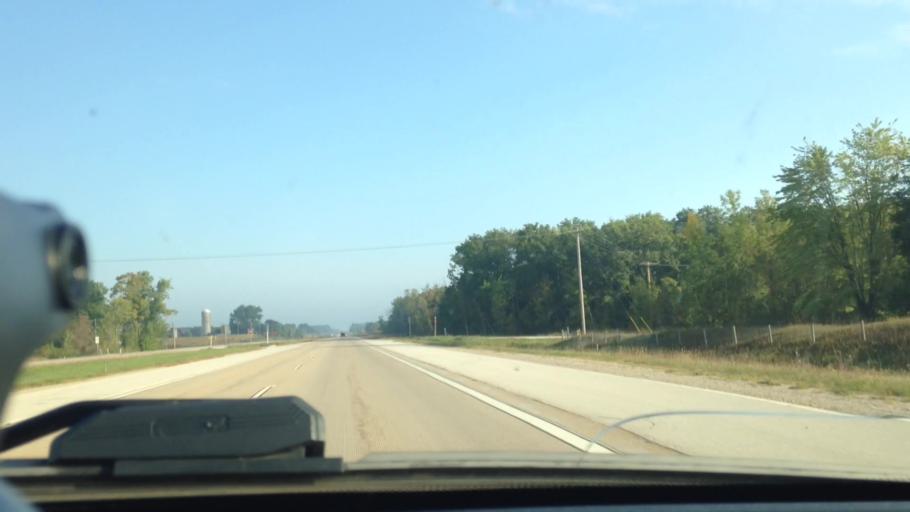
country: US
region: Wisconsin
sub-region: Oconto County
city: Oconto Falls
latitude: 45.0002
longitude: -88.0447
